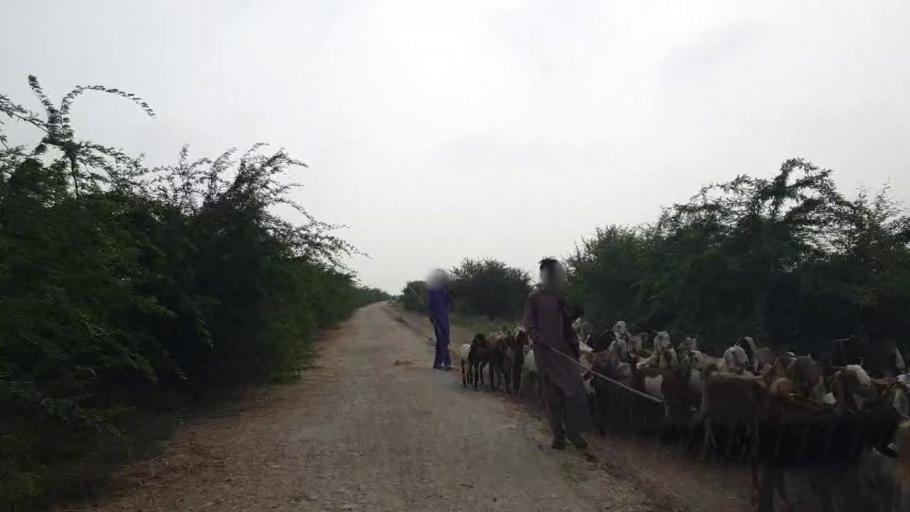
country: PK
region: Sindh
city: Kario
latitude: 24.8582
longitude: 68.5242
